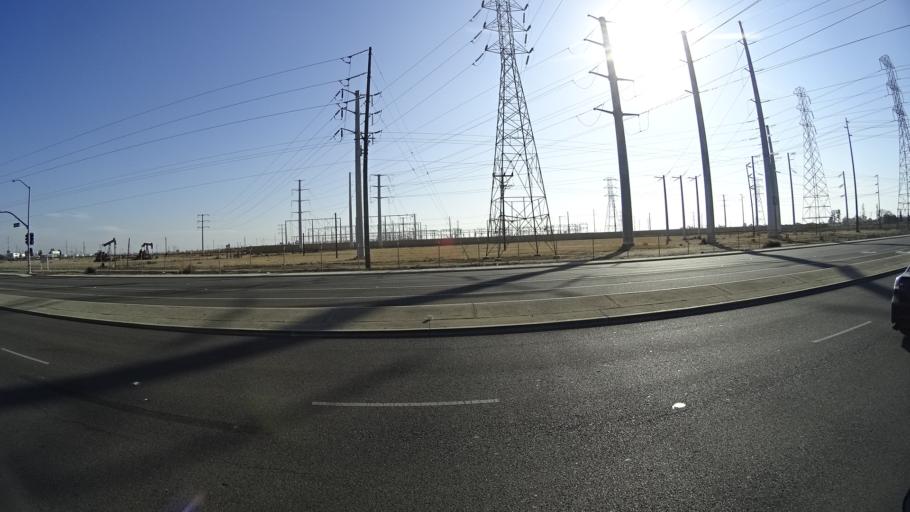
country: US
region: California
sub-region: Kern County
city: Greenacres
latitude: 35.3836
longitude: -119.0966
